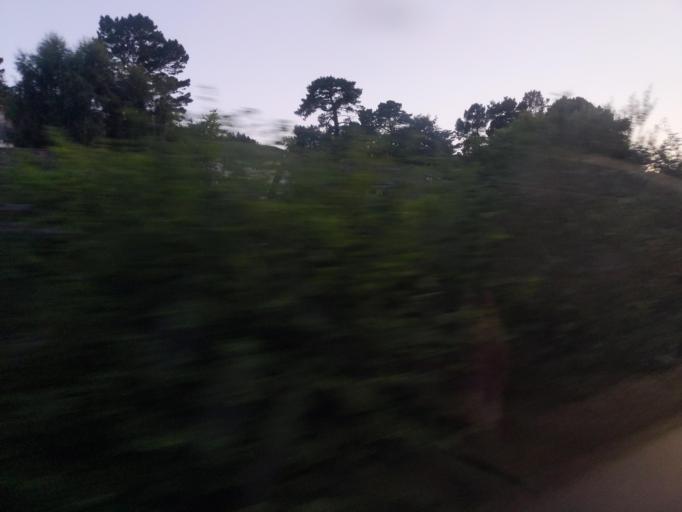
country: GB
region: England
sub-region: Devon
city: Totnes
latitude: 50.4326
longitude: -3.7056
